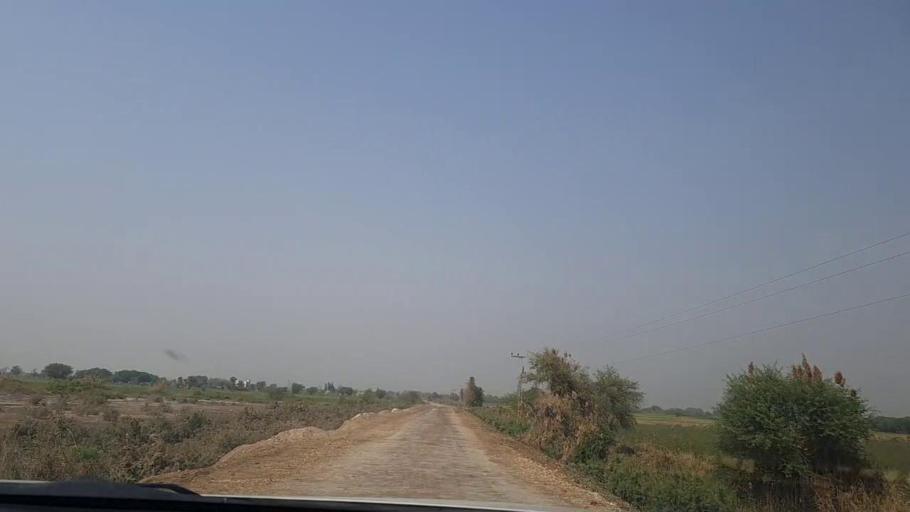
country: PK
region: Sindh
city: Pithoro
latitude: 25.5727
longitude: 69.2040
